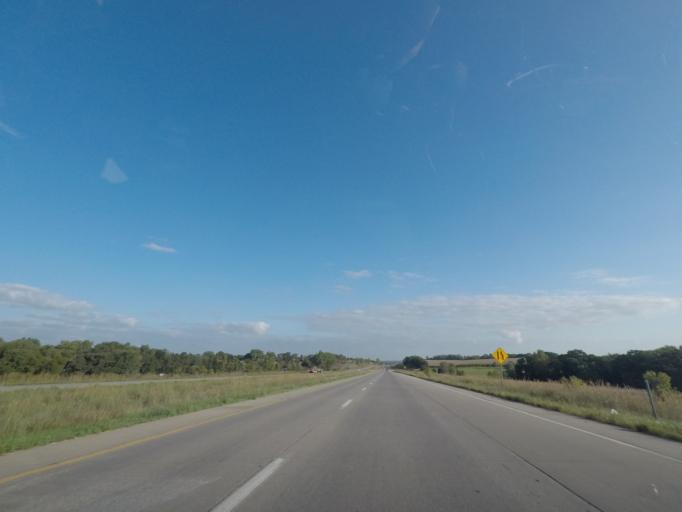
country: US
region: Iowa
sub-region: Warren County
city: Carlisle
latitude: 41.5259
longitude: -93.5193
